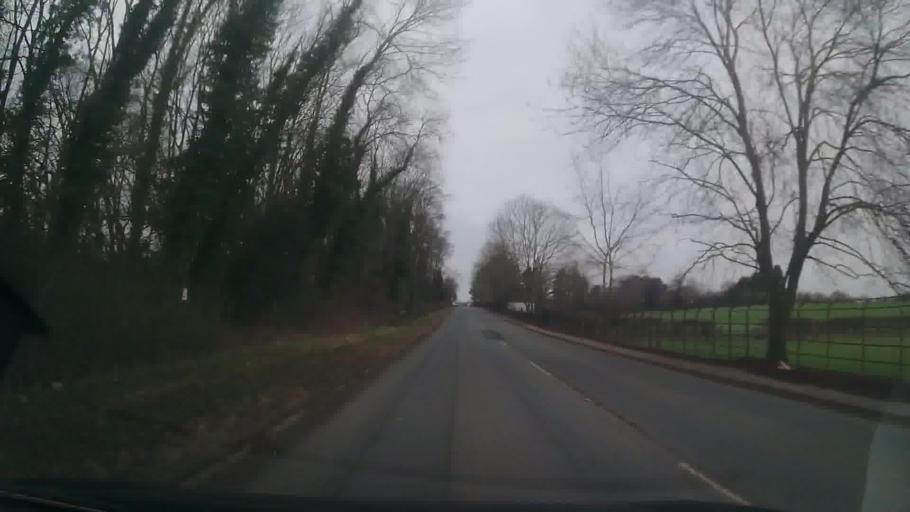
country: GB
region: England
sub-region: Shropshire
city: Bicton
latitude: 52.7221
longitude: -2.8041
